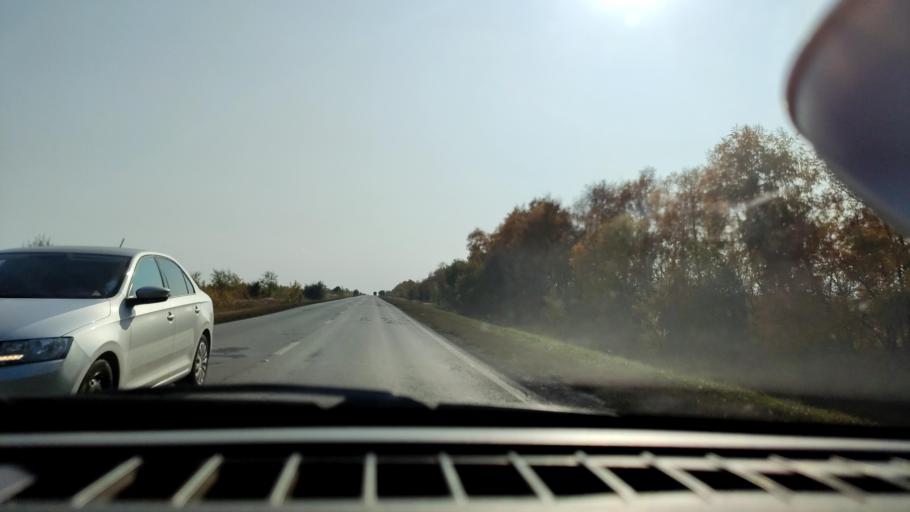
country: RU
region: Samara
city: Smyshlyayevka
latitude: 53.1317
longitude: 50.3708
